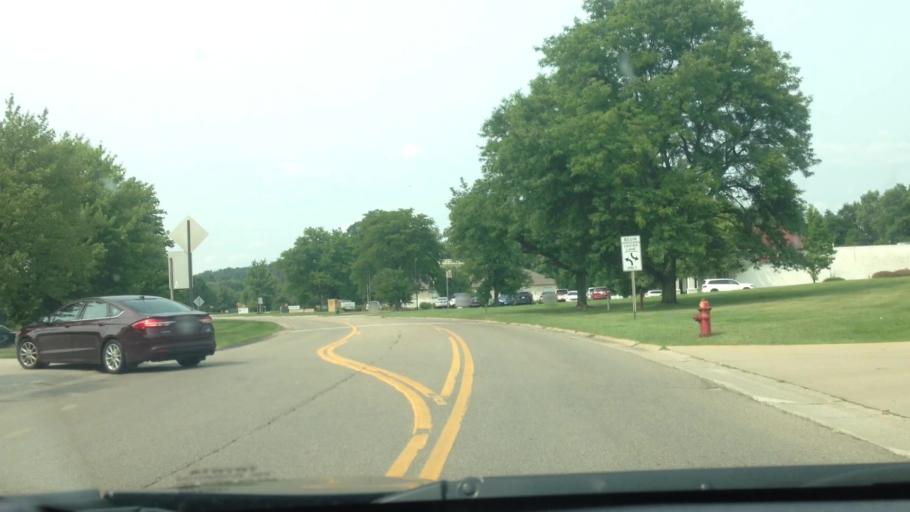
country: US
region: Ohio
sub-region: Summit County
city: Montrose-Ghent
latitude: 41.1366
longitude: -81.6450
